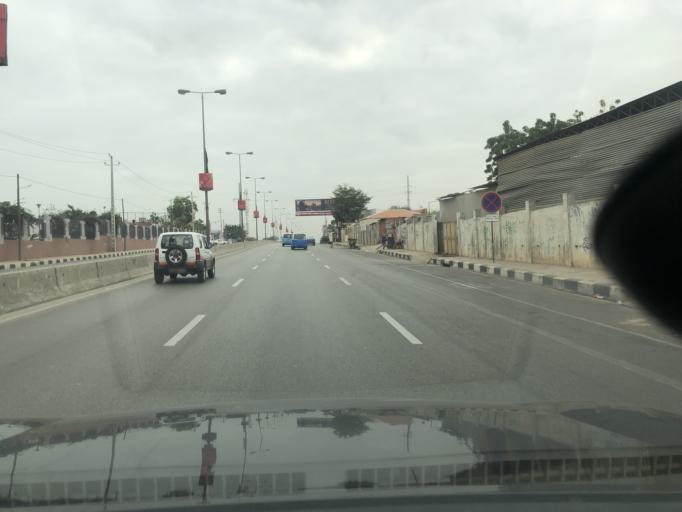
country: AO
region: Luanda
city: Luanda
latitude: -8.8876
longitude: 13.1816
